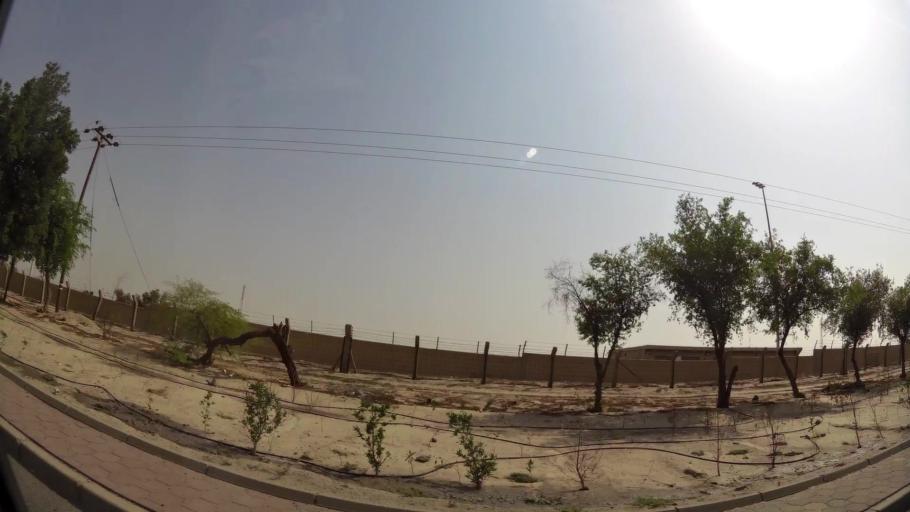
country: KW
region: Muhafazat al Jahra'
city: Al Jahra'
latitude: 29.3275
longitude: 47.7032
